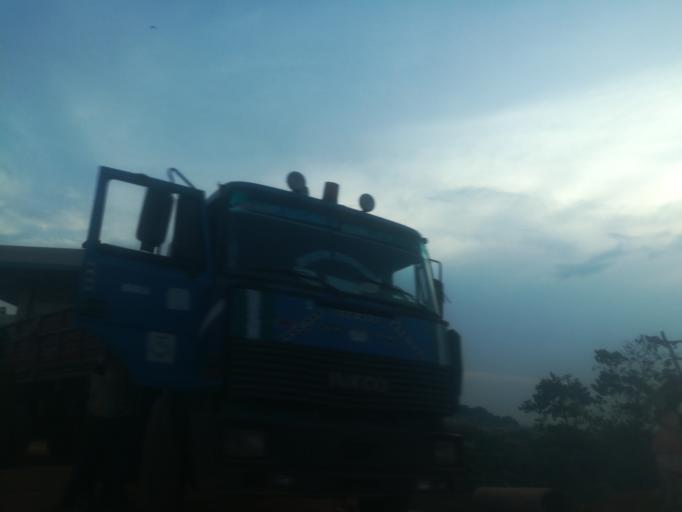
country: NG
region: Ogun
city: Abeokuta
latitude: 7.1811
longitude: 3.3501
